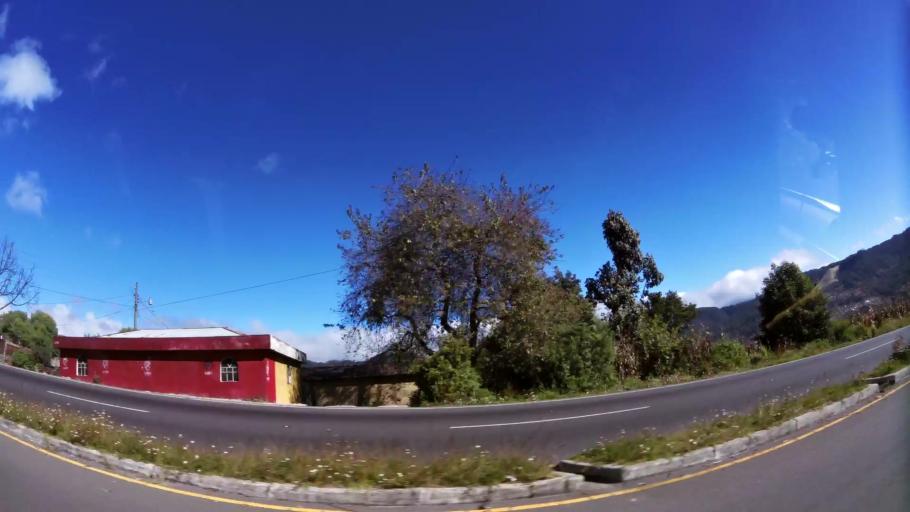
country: GT
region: Solola
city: Nahuala
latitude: 14.8265
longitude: -91.3322
